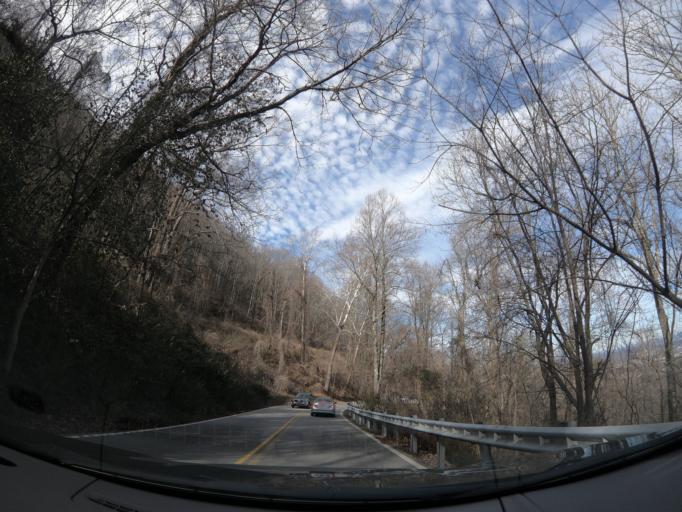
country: US
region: Tennessee
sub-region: Hamilton County
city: Lookout Mountain
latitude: 34.9985
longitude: -85.3417
